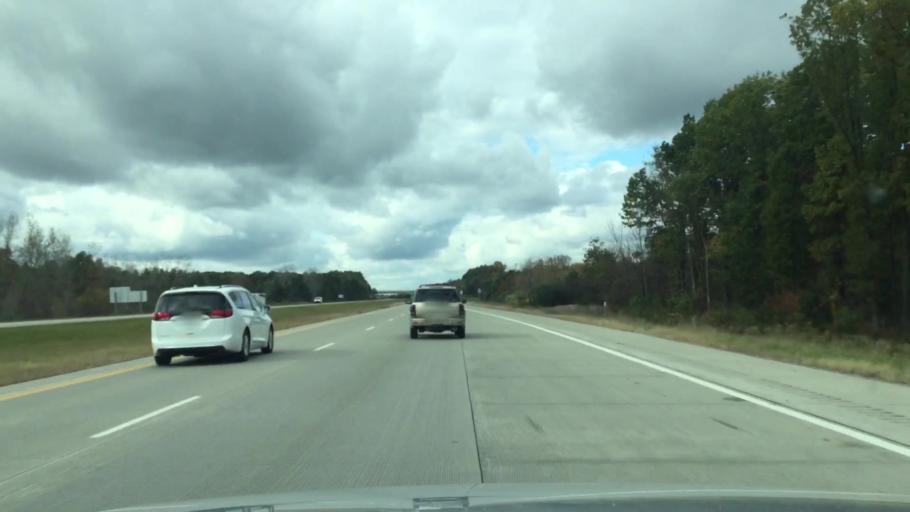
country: US
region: Michigan
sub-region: Lapeer County
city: Lapeer
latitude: 43.0310
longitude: -83.3694
